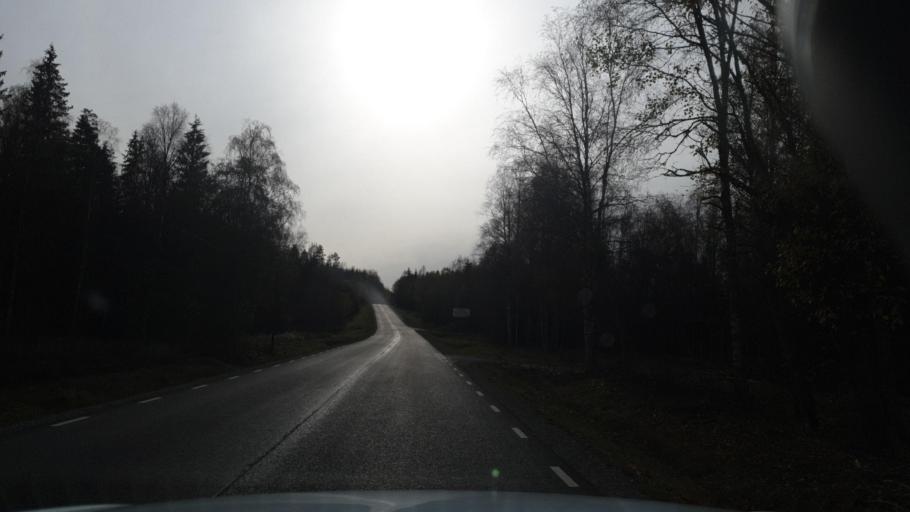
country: SE
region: Vaermland
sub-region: Arjangs Kommun
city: Arjaeng
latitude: 59.5779
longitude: 12.1235
